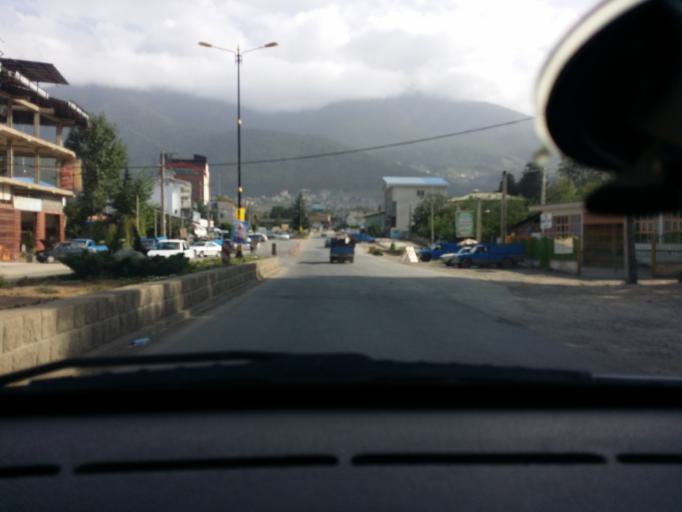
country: IR
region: Mazandaran
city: `Abbasabad
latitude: 36.5076
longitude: 51.1584
